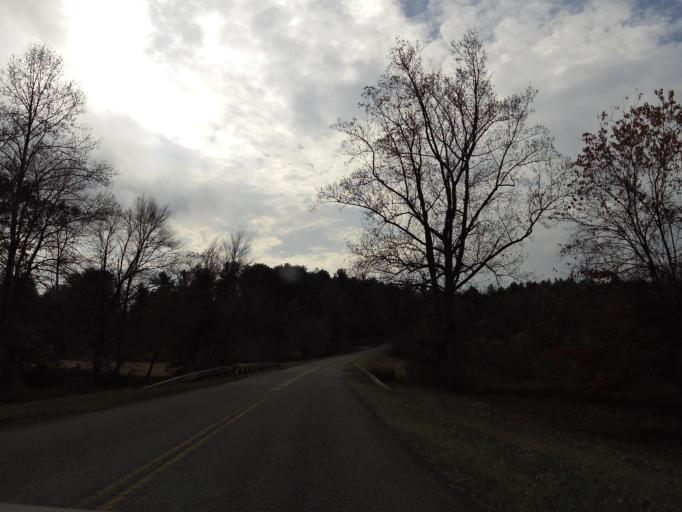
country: US
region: Virginia
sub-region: City of Galax
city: Galax
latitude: 36.5705
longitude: -80.8585
